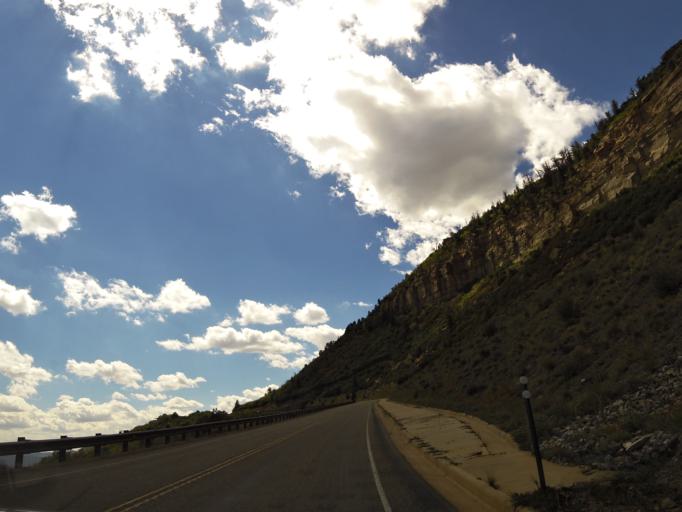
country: US
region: Colorado
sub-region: Montezuma County
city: Mancos
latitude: 37.3083
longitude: -108.4131
